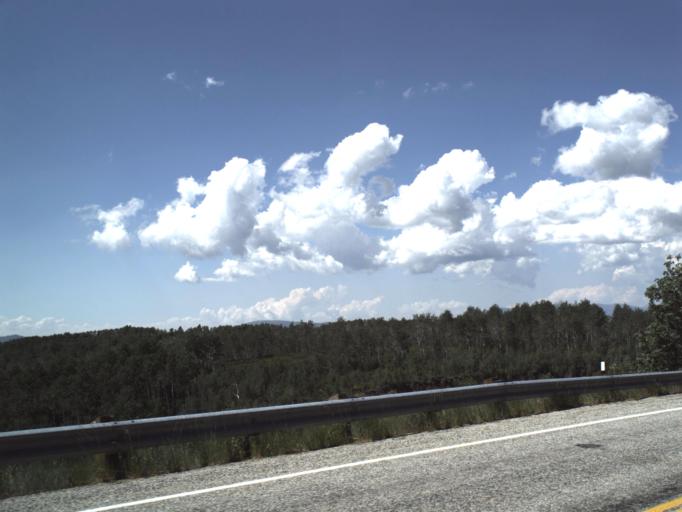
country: US
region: Utah
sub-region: Weber County
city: Wolf Creek
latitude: 41.4173
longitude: -111.5628
